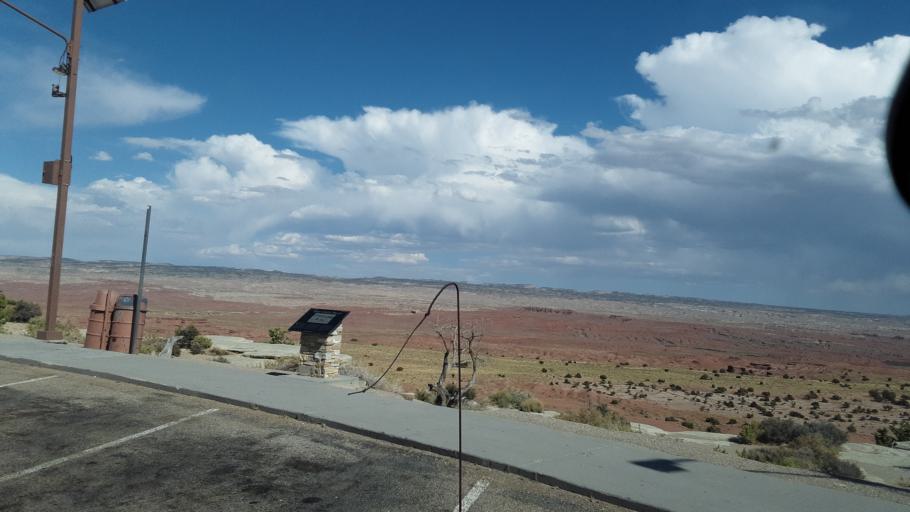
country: US
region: Utah
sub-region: Emery County
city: Ferron
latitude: 38.8287
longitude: -111.1148
